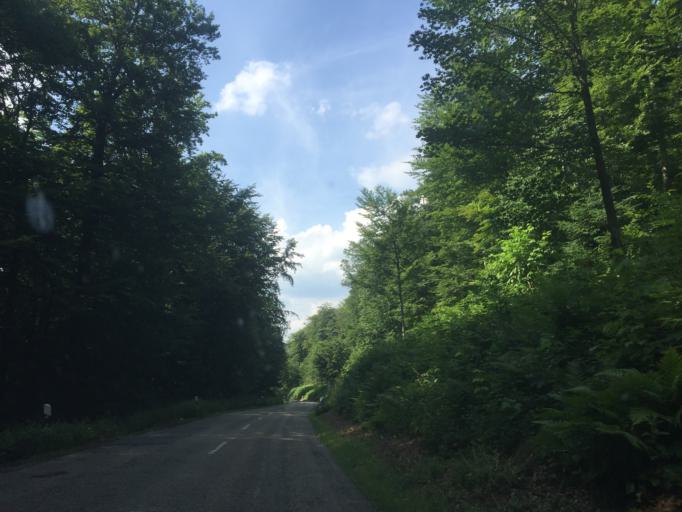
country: DE
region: Baden-Wuerttemberg
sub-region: Karlsruhe Region
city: Heidelberg
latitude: 49.3876
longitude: 8.7162
